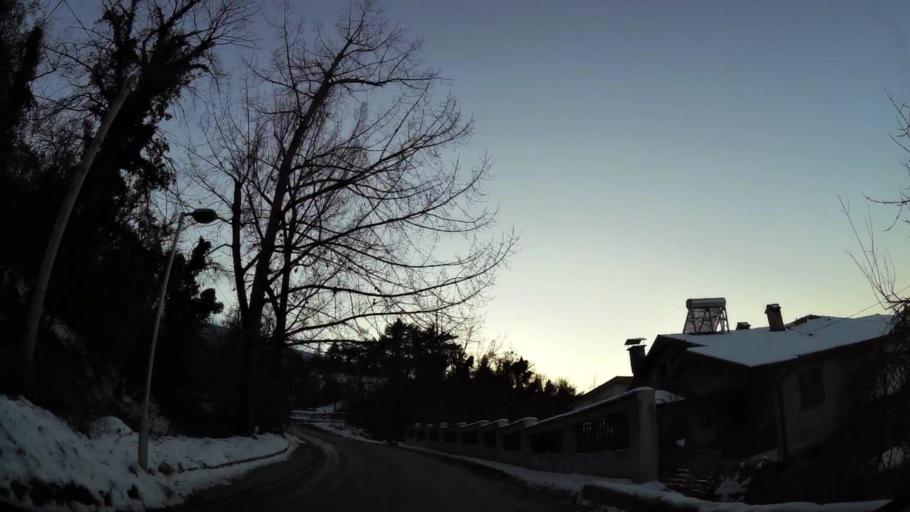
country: MK
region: Karpos
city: Skopje
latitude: 41.9918
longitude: 21.4062
